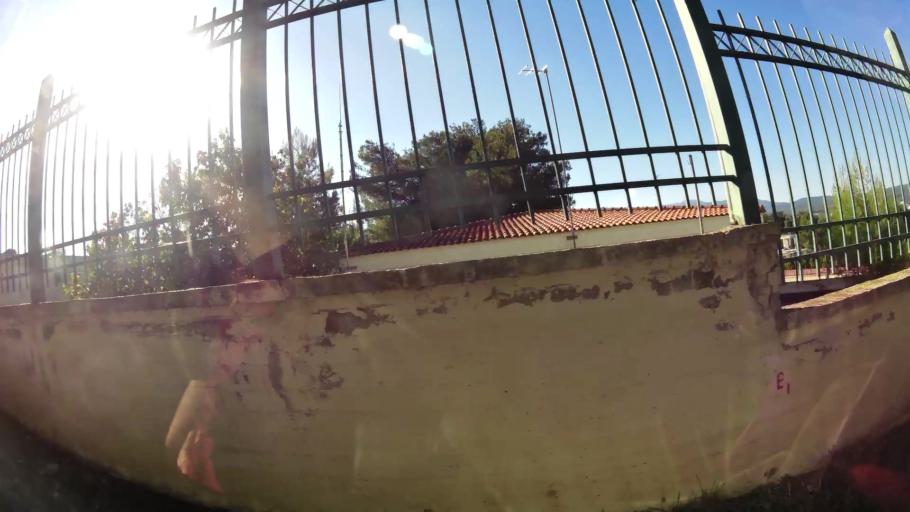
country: GR
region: Attica
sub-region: Nomarchia Anatolikis Attikis
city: Anoixi
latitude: 38.1235
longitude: 23.8531
